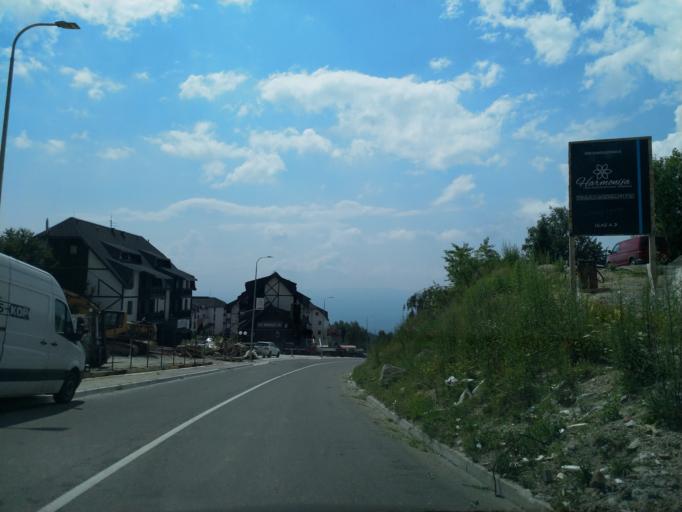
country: RS
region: Central Serbia
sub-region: Raski Okrug
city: Raska
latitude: 43.2755
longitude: 20.7613
